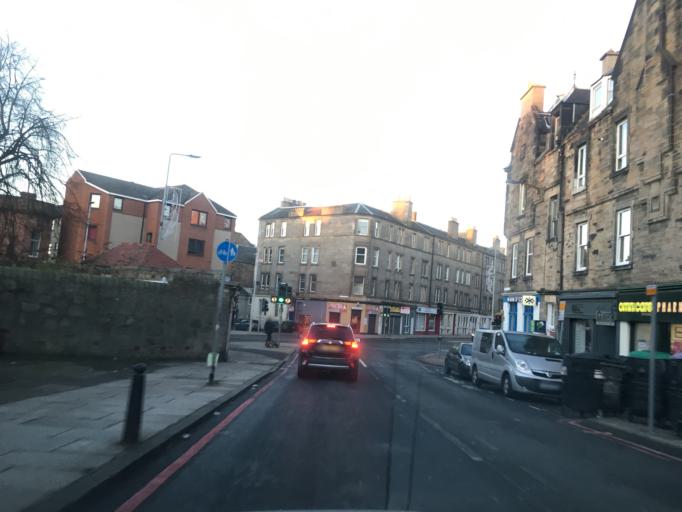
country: GB
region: Scotland
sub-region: Edinburgh
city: Edinburgh
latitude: 55.9387
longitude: -3.2264
